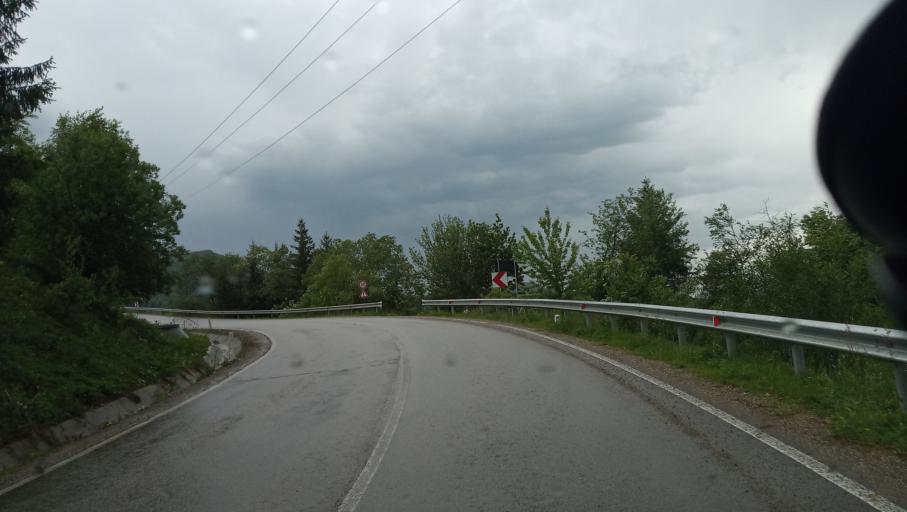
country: RO
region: Bistrita-Nasaud
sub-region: Comuna Tiha Bargaului
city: Tureac
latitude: 47.1897
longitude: 24.8860
